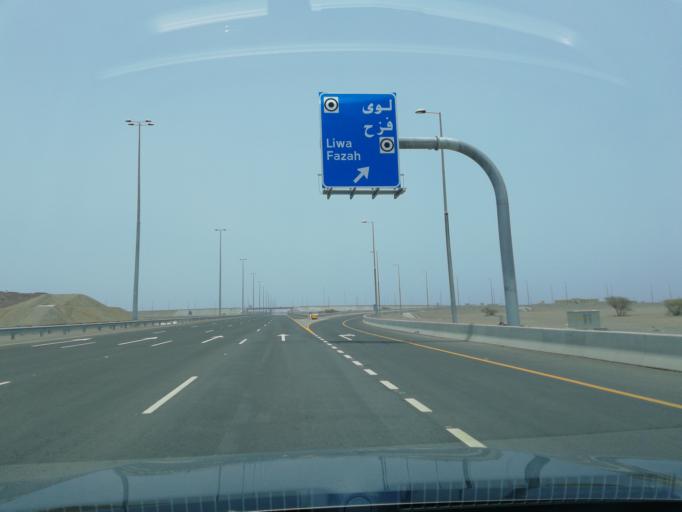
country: OM
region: Al Batinah
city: Al Liwa'
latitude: 24.5236
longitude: 56.5035
